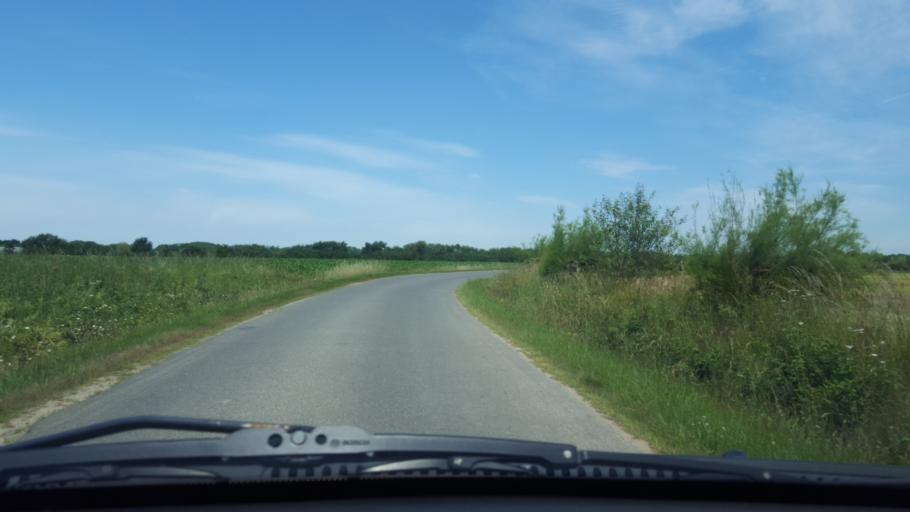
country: FR
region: Pays de la Loire
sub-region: Departement de la Loire-Atlantique
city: La Limouziniere
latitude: 47.0419
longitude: -1.5803
